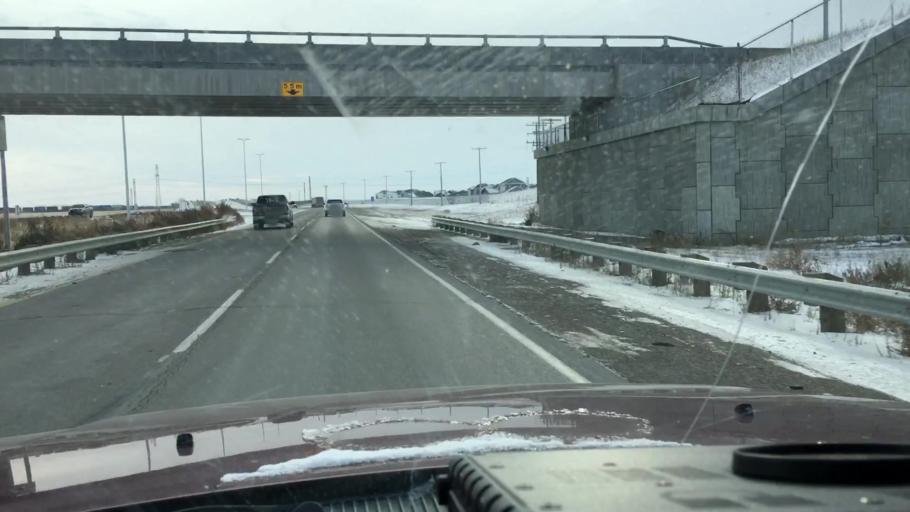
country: CA
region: Saskatchewan
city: Saskatoon
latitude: 52.0782
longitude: -106.6049
